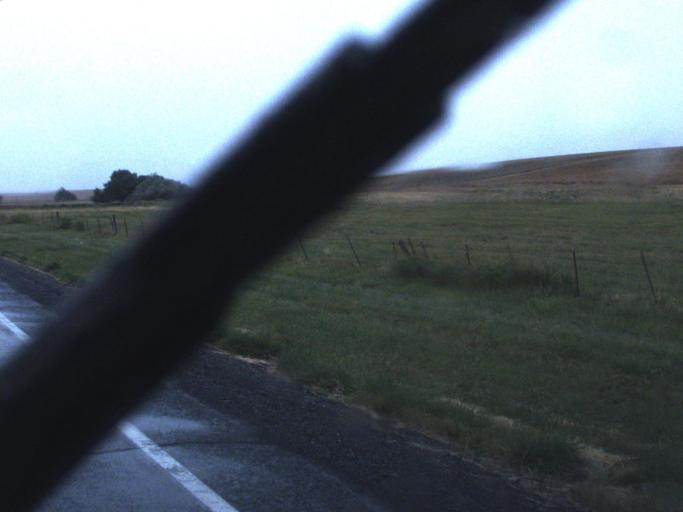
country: US
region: Washington
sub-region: Lincoln County
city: Davenport
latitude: 47.4526
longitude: -118.1858
